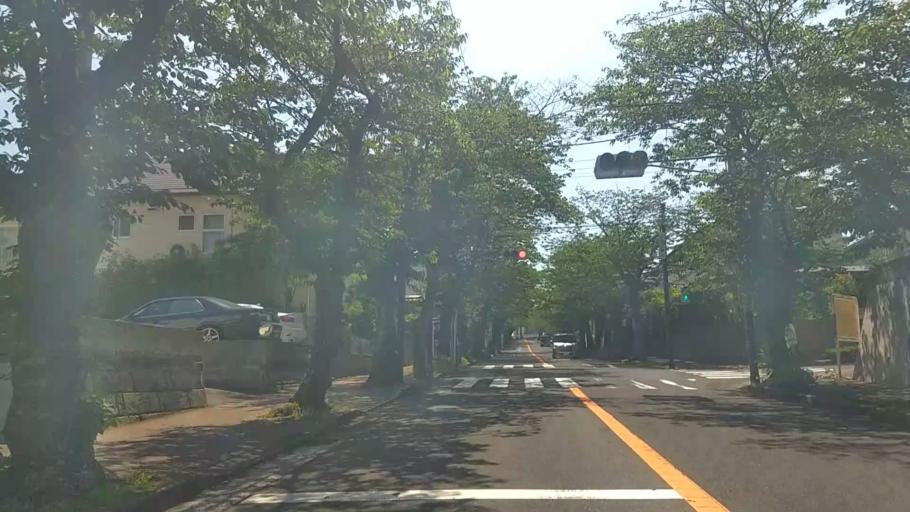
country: JP
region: Kanagawa
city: Zushi
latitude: 35.3087
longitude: 139.5751
